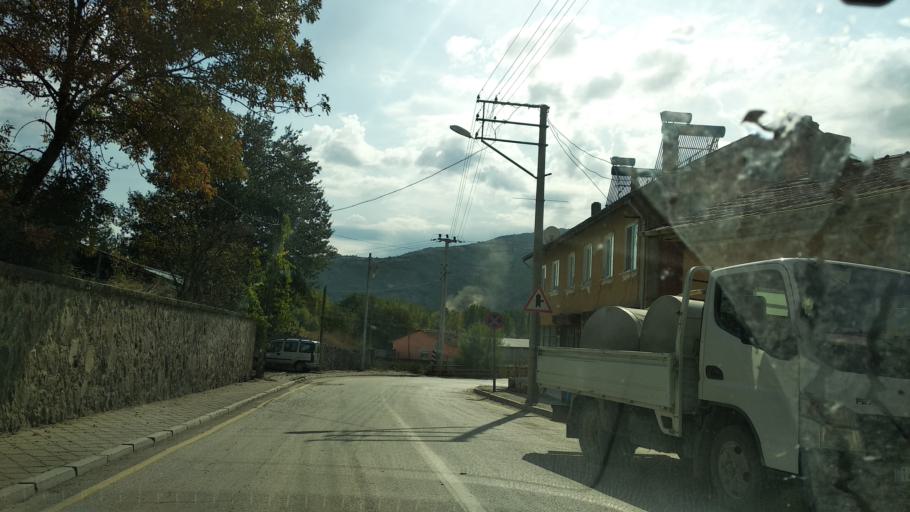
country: TR
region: Bolu
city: Seben
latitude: 40.4078
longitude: 31.5728
